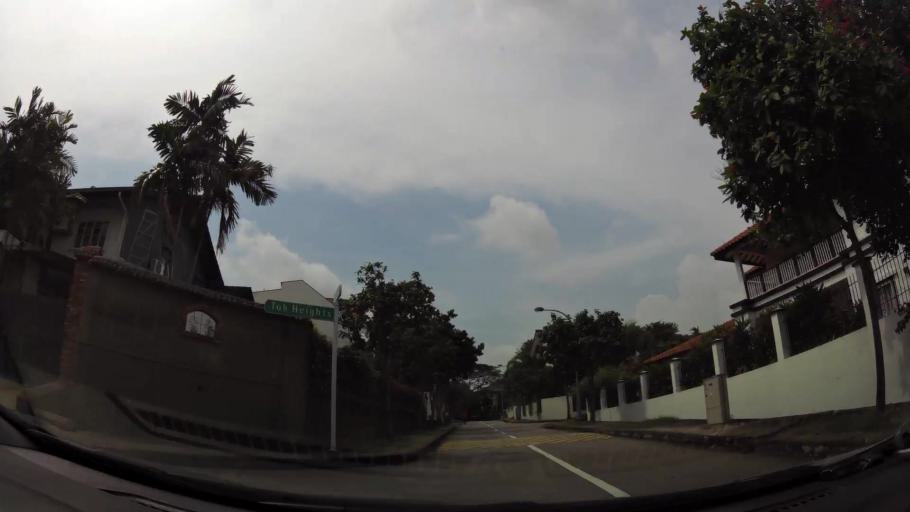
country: SG
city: Singapore
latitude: 1.3641
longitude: 103.9713
